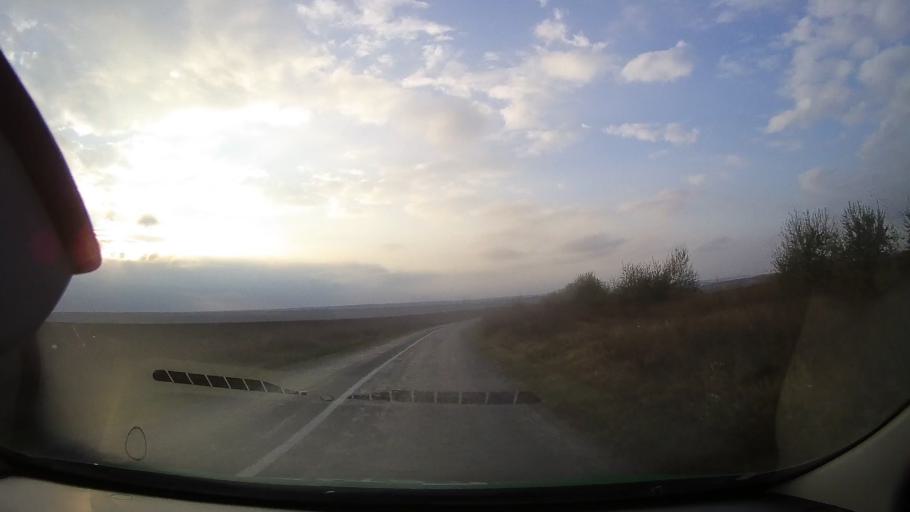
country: RO
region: Constanta
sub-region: Comuna Adamclisi
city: Adamclisi
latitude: 44.0165
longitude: 27.8951
